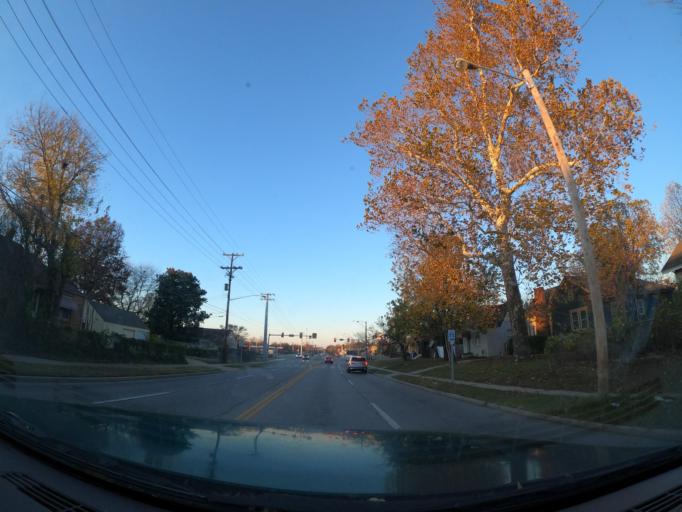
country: US
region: Oklahoma
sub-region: Tulsa County
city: Tulsa
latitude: 36.1583
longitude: -95.9403
